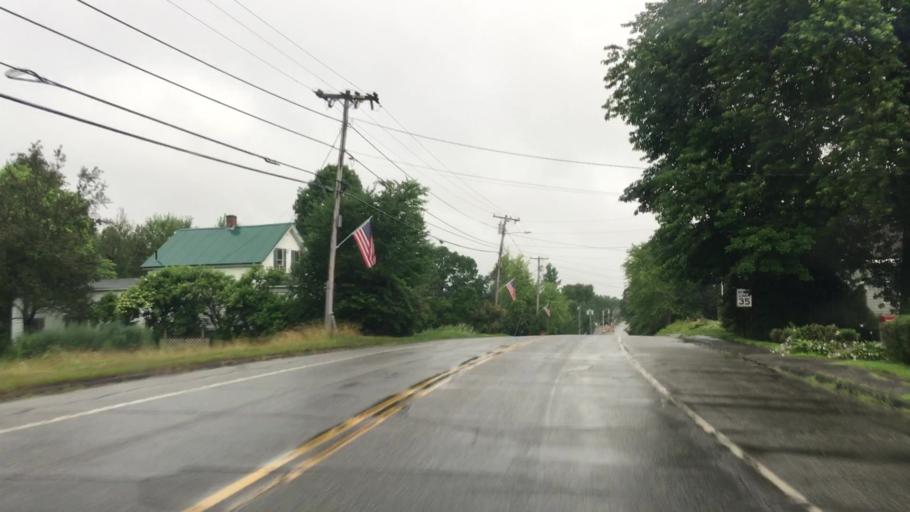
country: US
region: Maine
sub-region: Kennebec County
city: Pittston
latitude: 44.1893
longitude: -69.7573
